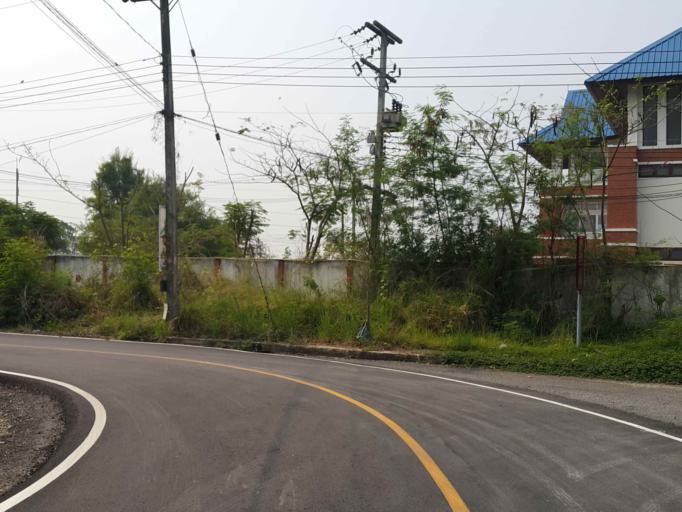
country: TH
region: Chiang Mai
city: Saraphi
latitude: 18.7566
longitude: 99.0598
